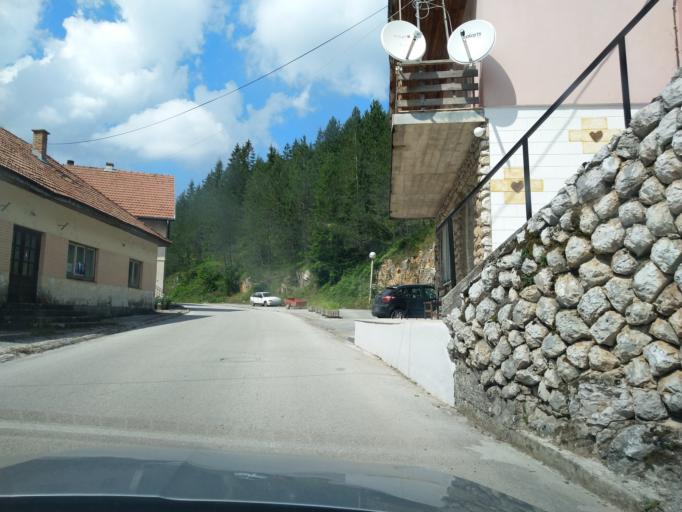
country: RS
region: Central Serbia
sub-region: Zlatiborski Okrug
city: Nova Varos
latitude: 43.5480
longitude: 19.9028
